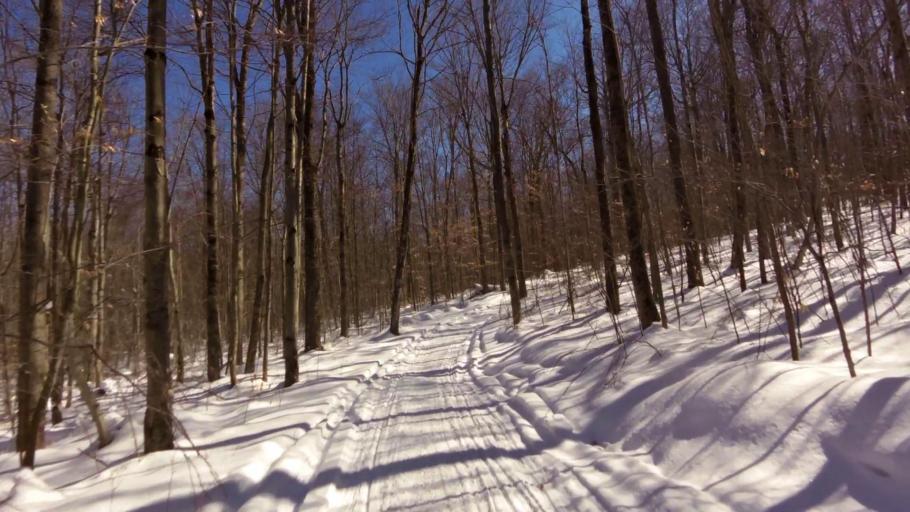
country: US
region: New York
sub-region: Allegany County
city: Houghton
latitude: 42.3633
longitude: -78.1883
